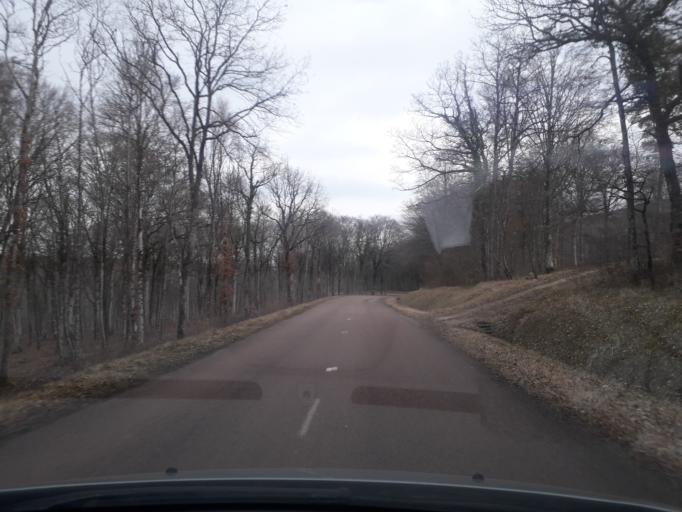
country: FR
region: Bourgogne
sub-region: Departement de la Cote-d'Or
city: Messigny-et-Vantoux
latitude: 47.4721
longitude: 4.9499
